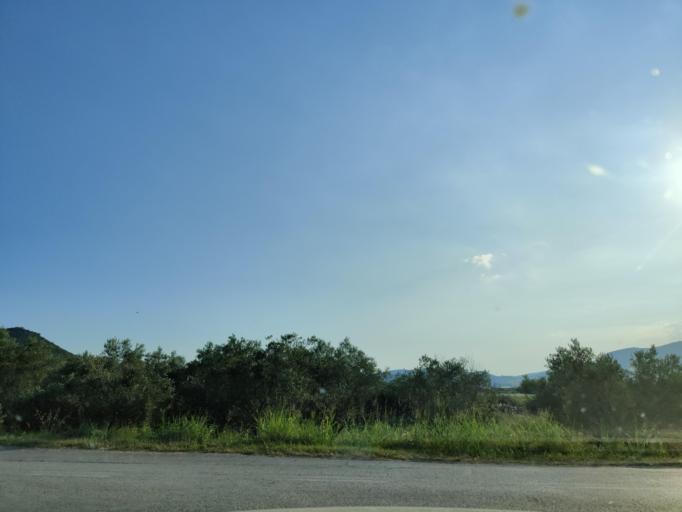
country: GR
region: East Macedonia and Thrace
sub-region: Nomos Kavalas
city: Nea Peramos
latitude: 40.8282
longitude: 24.2955
